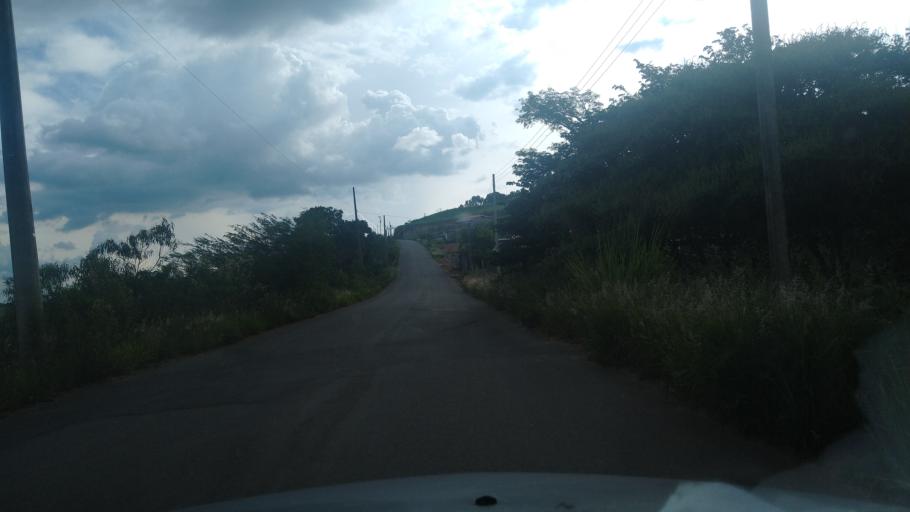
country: BR
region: Minas Gerais
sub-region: Extrema
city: Extrema
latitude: -22.7330
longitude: -46.3639
